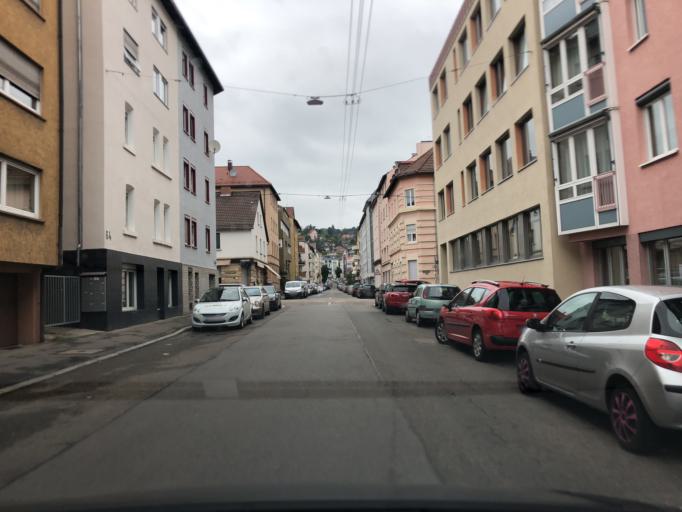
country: DE
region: Baden-Wuerttemberg
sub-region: Regierungsbezirk Stuttgart
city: Stuttgart
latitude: 48.7809
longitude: 9.1616
